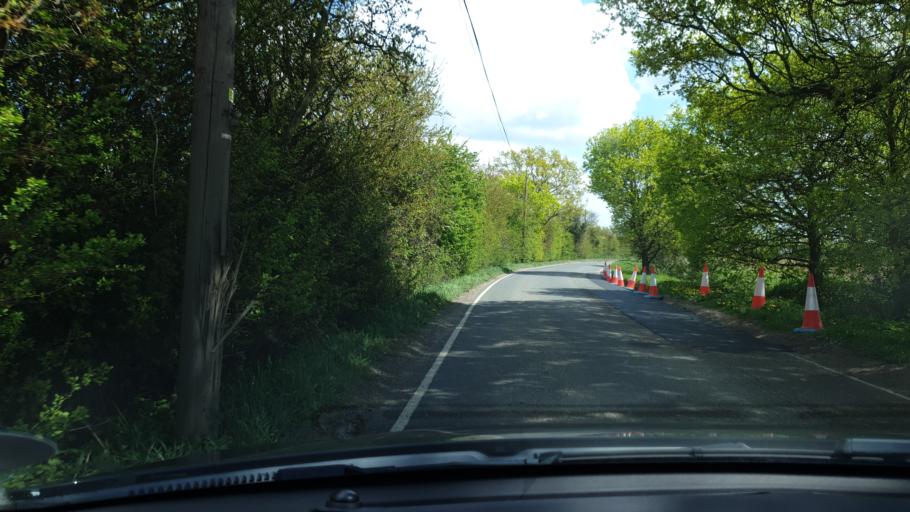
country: GB
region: England
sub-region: Essex
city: Little Clacton
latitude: 51.8652
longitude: 1.1801
